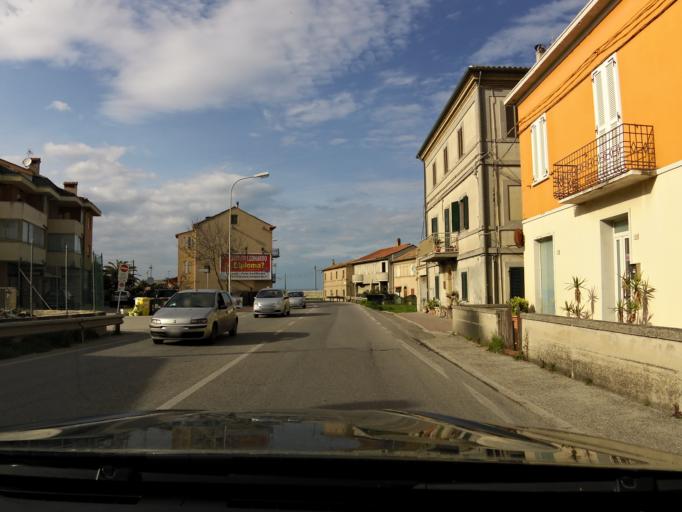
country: IT
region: The Marches
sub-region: Provincia di Macerata
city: Civitanova Marche
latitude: 43.3306
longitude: 13.7124
